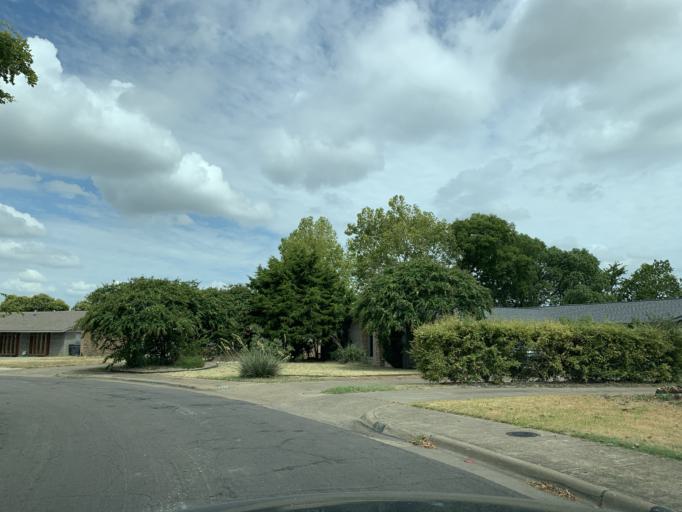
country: US
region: Texas
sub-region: Dallas County
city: Cockrell Hill
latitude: 32.7634
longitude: -96.8632
